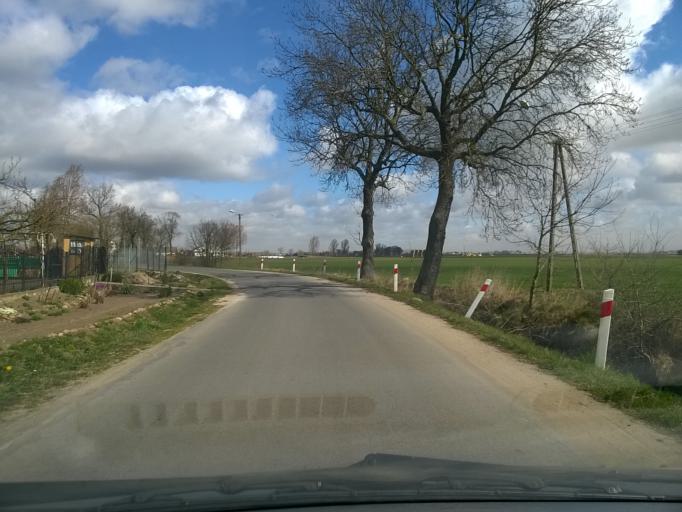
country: PL
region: Kujawsko-Pomorskie
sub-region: Powiat nakielski
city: Kcynia
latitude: 52.9902
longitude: 17.4302
